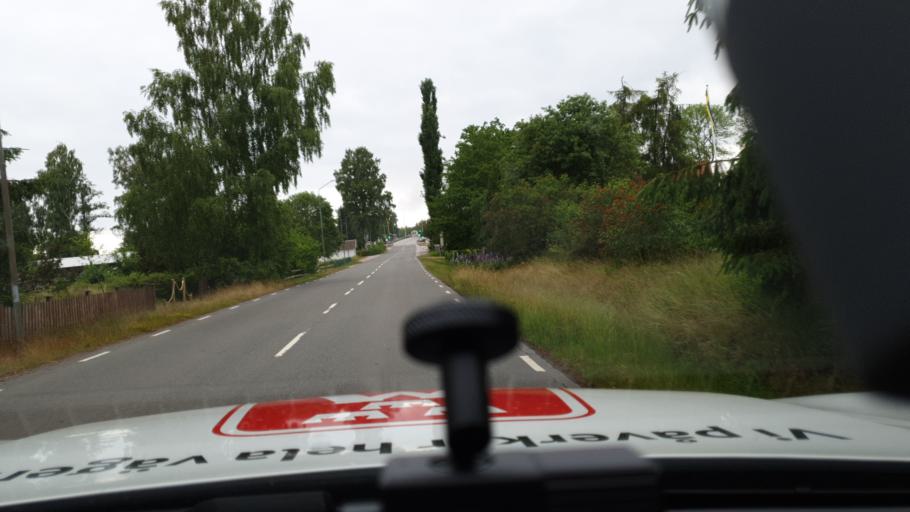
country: SE
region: Vaestra Goetaland
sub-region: Gullspangs Kommun
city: Gullspang
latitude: 58.8341
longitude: 13.9813
